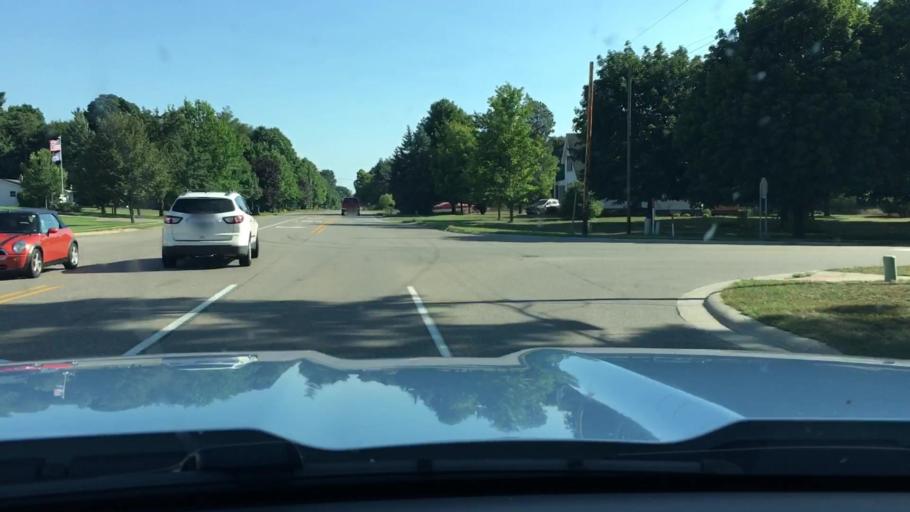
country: US
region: Michigan
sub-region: Ottawa County
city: Allendale
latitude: 42.9579
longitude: -85.9535
